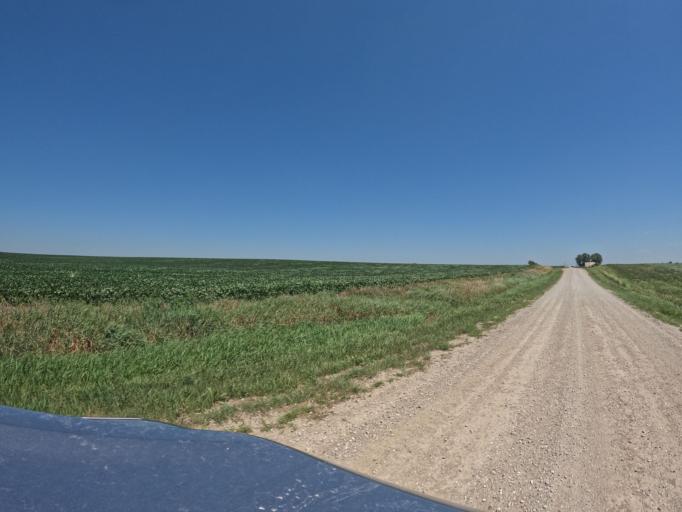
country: US
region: Iowa
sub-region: Keokuk County
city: Sigourney
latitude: 41.4235
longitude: -92.3276
